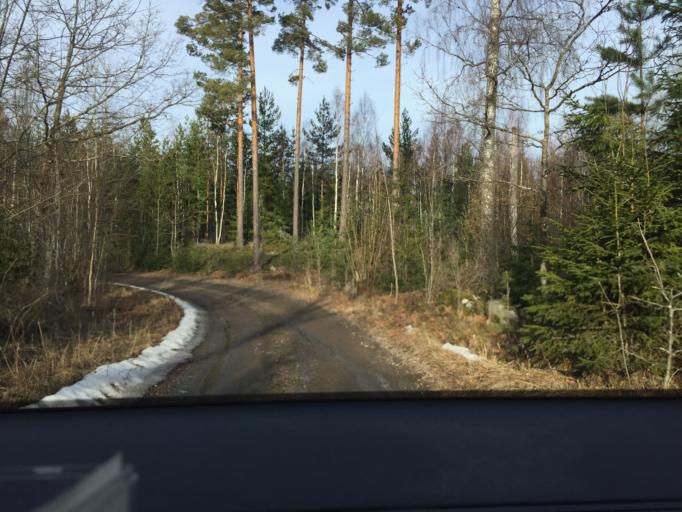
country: SE
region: OErebro
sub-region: Orebro Kommun
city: Odensbacken
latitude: 59.1161
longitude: 15.4522
